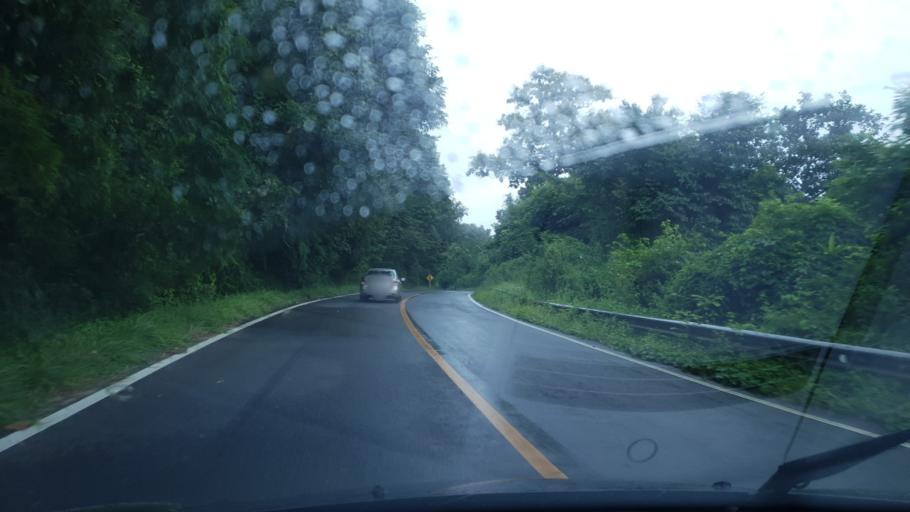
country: TH
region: Mae Hong Son
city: Khun Yuam
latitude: 18.6777
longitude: 97.9227
